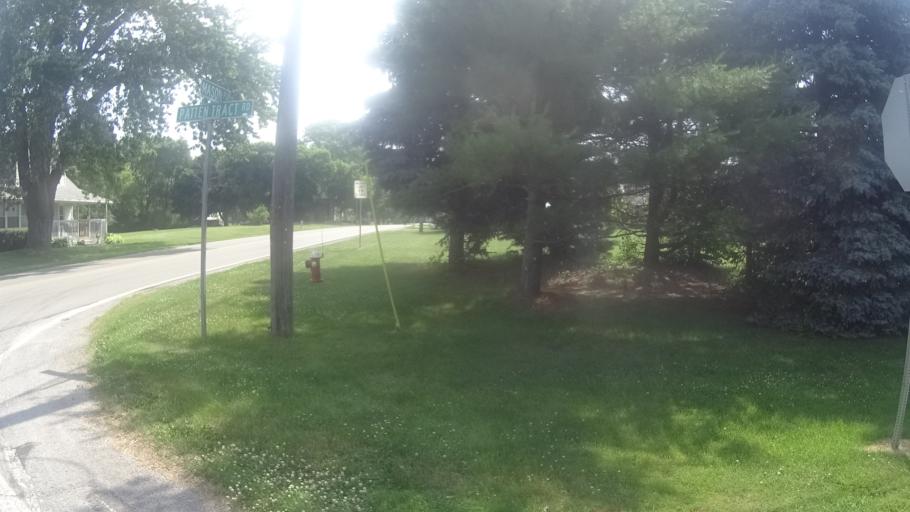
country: US
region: Ohio
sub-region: Erie County
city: Sandusky
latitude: 41.3550
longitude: -82.7273
